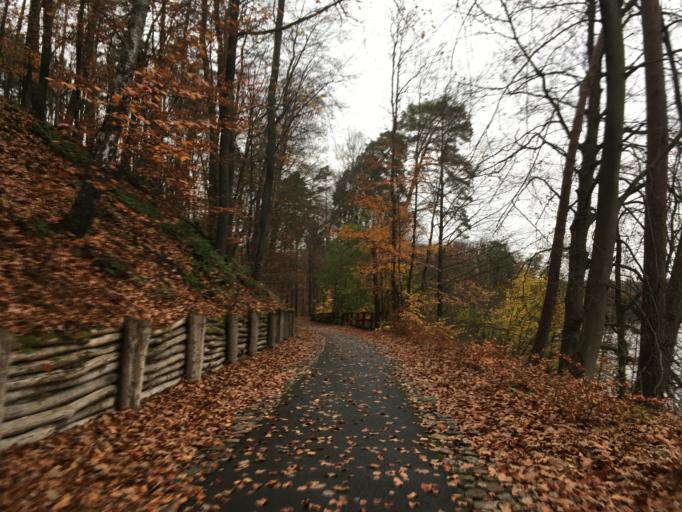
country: DE
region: Brandenburg
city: Mixdorf
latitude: 52.1602
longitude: 14.4433
